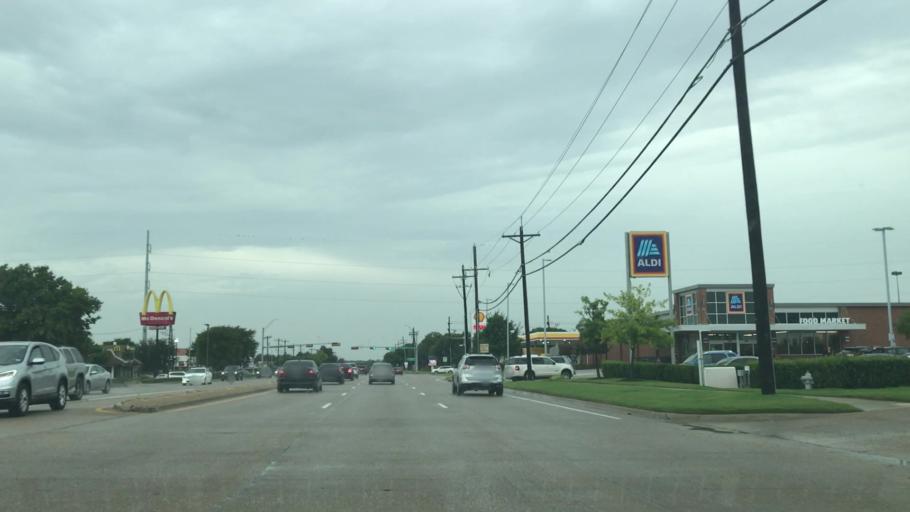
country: US
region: Texas
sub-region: Denton County
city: Lewisville
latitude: 33.0424
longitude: -97.0341
